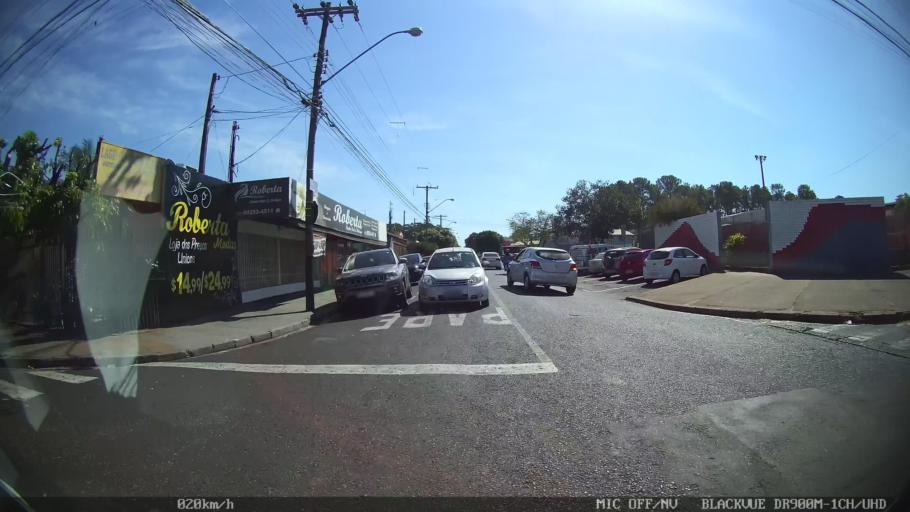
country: BR
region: Sao Paulo
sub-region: Sao Jose Do Rio Preto
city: Sao Jose do Rio Preto
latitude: -20.7809
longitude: -49.4089
